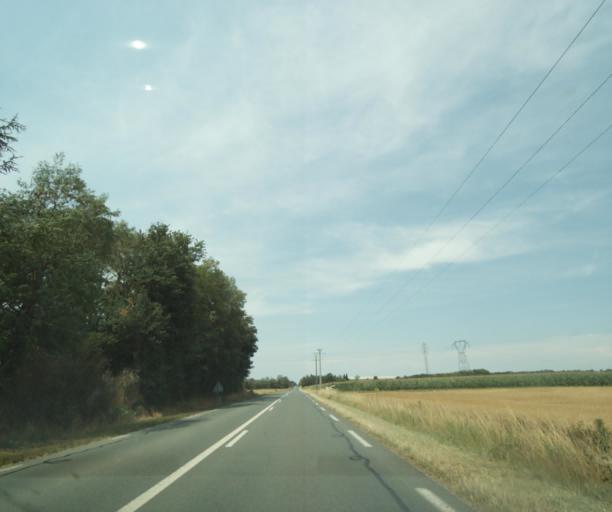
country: FR
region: Poitou-Charentes
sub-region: Departement de la Vienne
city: Cenon-sur-Vienne
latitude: 46.7536
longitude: 0.5544
